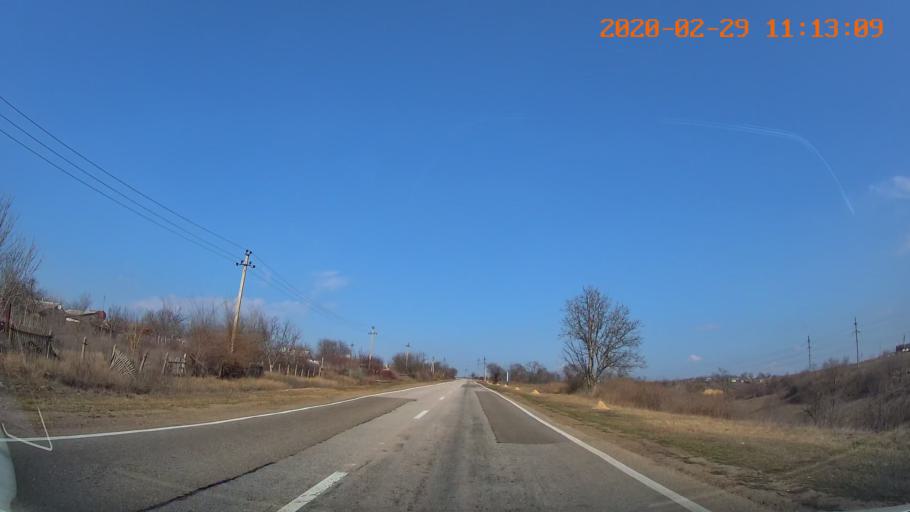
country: MD
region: Telenesti
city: Dubasari
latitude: 47.2690
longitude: 29.1818
